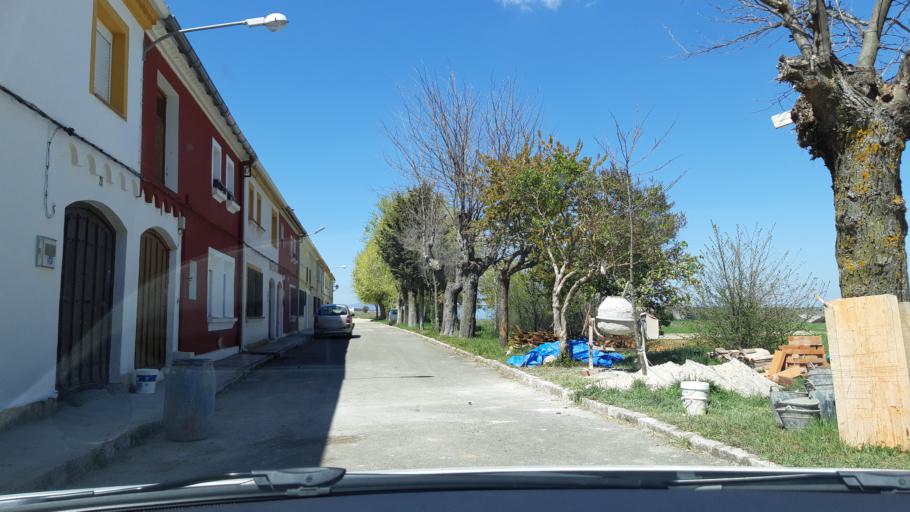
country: ES
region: Castille-La Mancha
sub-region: Provincia de Guadalajara
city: Gajanejos
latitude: 40.8415
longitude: -2.8914
